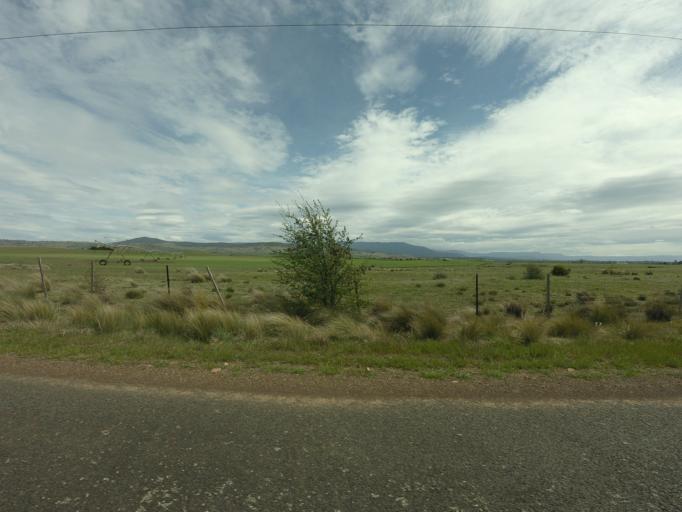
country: AU
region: Tasmania
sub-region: Northern Midlands
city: Evandale
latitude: -41.8731
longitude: 147.3538
